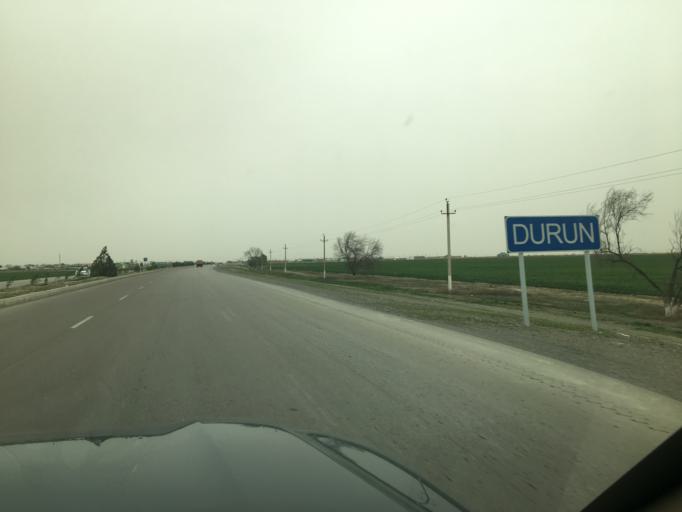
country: TM
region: Ahal
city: Baharly
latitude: 38.3906
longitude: 57.4864
